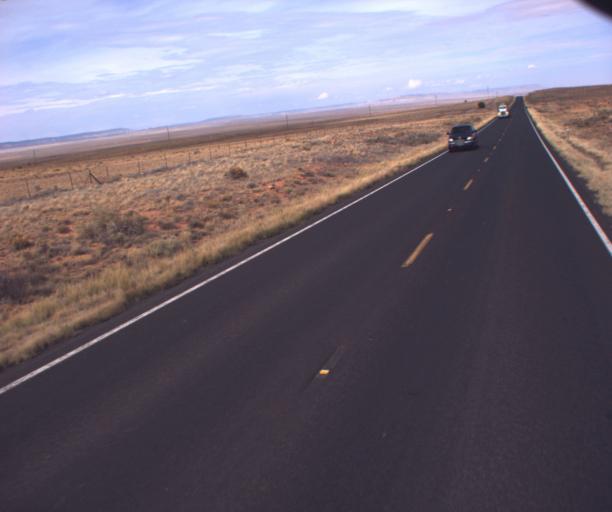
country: US
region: Arizona
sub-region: Apache County
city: Ganado
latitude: 35.8750
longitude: -109.6003
